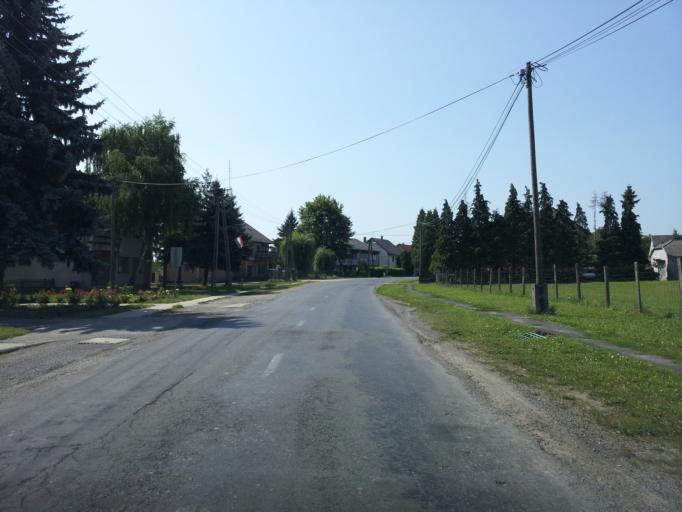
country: HU
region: Zala
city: Zalaszentgrot
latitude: 46.8431
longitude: 17.0946
